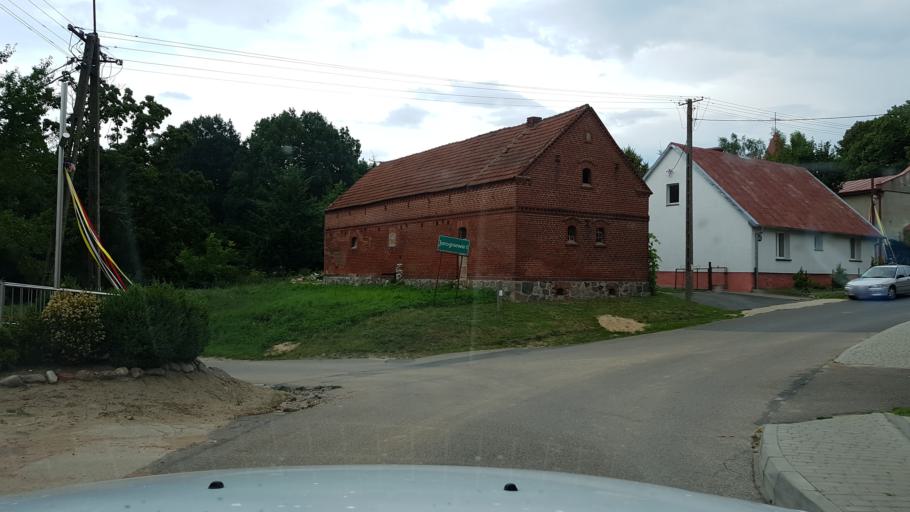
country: PL
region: West Pomeranian Voivodeship
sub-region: Powiat walecki
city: Walcz
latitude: 53.3531
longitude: 16.3959
